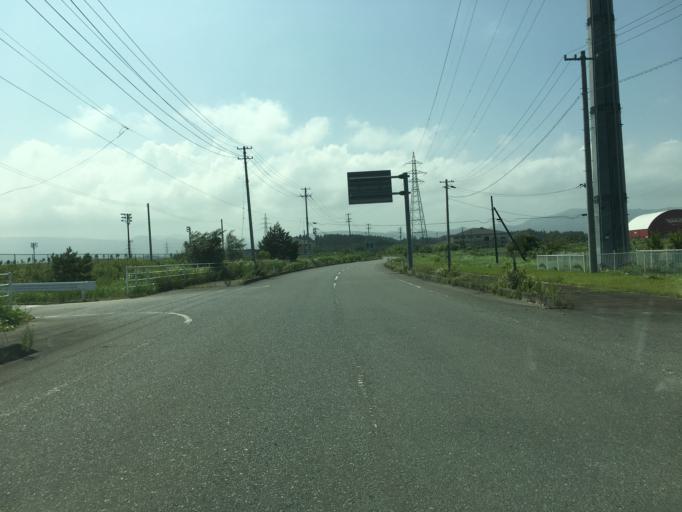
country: JP
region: Miyagi
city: Marumori
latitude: 37.8331
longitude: 140.9375
